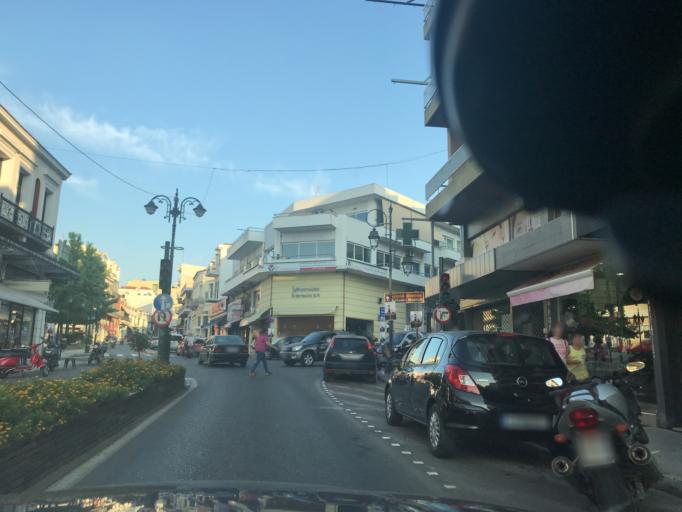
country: GR
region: West Greece
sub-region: Nomos Ileias
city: Pyrgos
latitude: 37.6736
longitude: 21.4368
